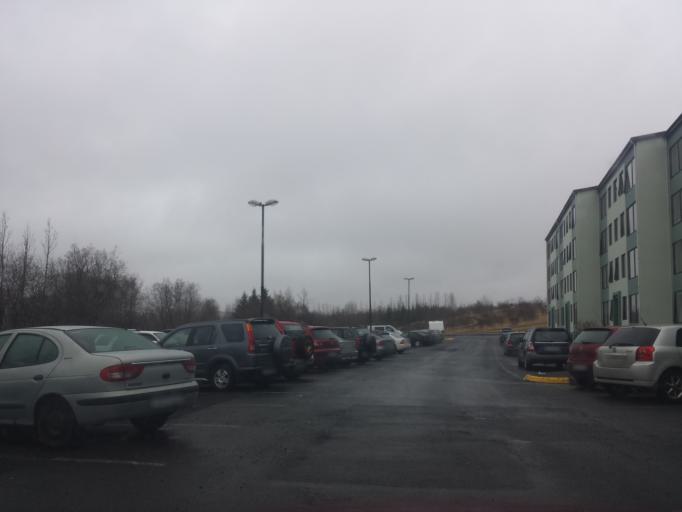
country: IS
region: Capital Region
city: Reykjavik
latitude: 64.1138
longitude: -21.8559
